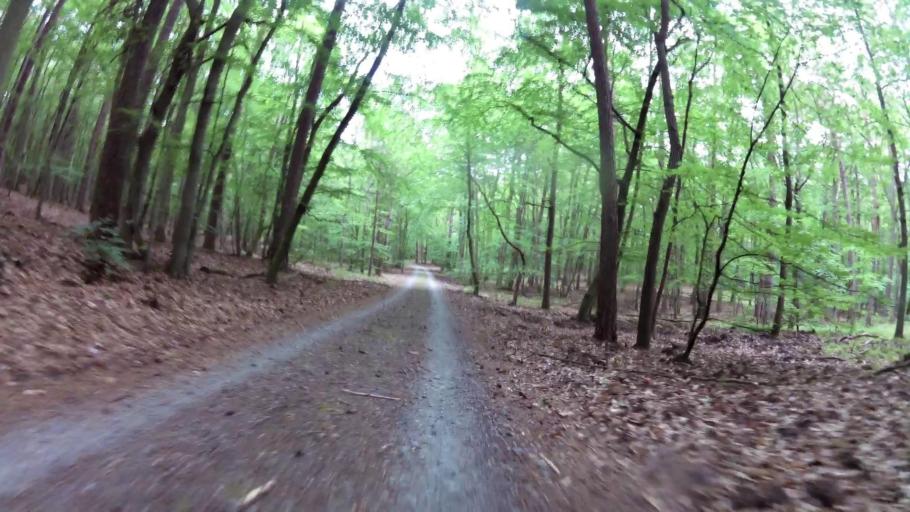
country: PL
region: West Pomeranian Voivodeship
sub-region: Powiat kamienski
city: Miedzyzdroje
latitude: 53.9363
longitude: 14.4917
